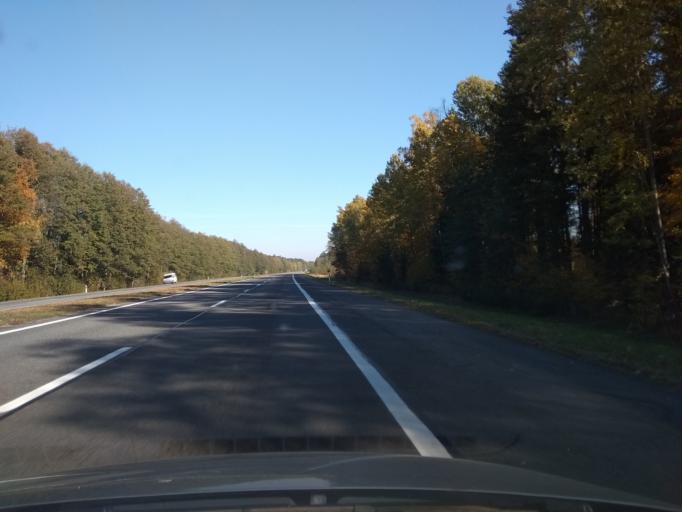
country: BY
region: Brest
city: Nyakhachava
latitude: 52.6439
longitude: 25.2378
